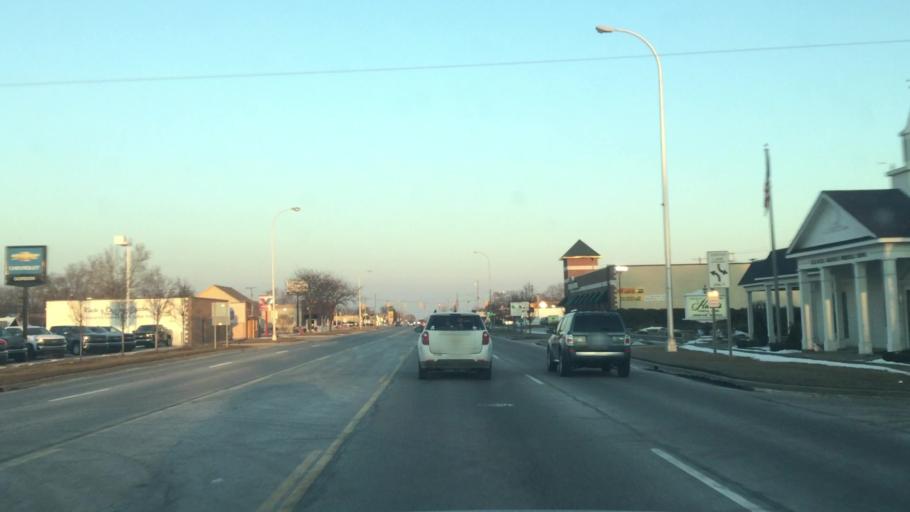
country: US
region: Michigan
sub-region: Wayne County
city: Garden City
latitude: 42.3251
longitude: -83.3535
